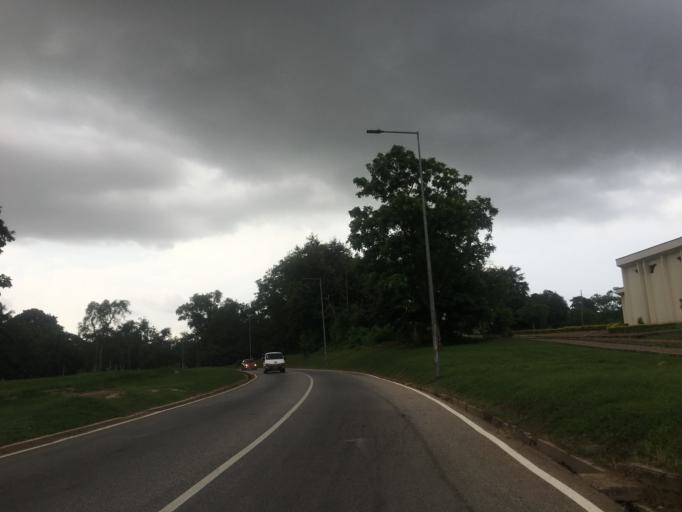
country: GH
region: Ashanti
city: Kumasi
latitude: 6.6810
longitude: -1.5699
